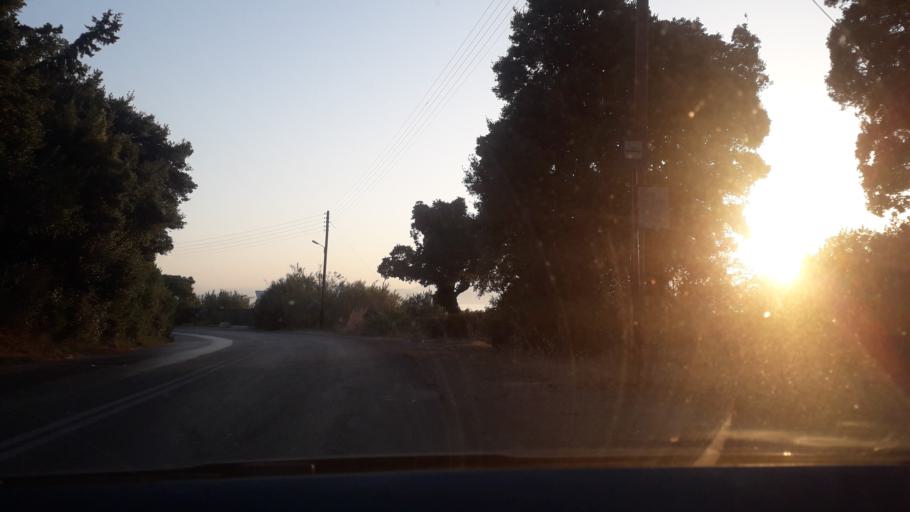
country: GR
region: Ionian Islands
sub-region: Nomos Kerkyras
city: Kynopiastes
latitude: 39.5382
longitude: 19.9171
